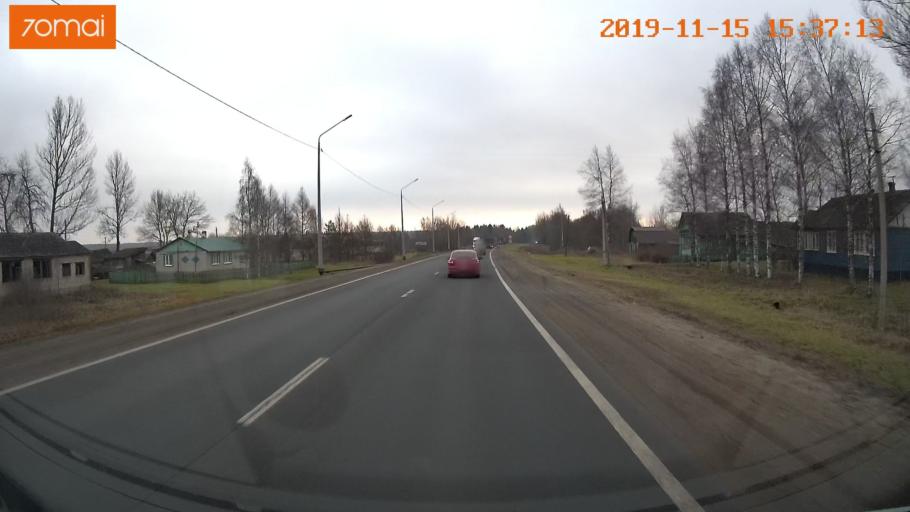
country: RU
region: Jaroslavl
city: Danilov
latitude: 58.0417
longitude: 40.0895
